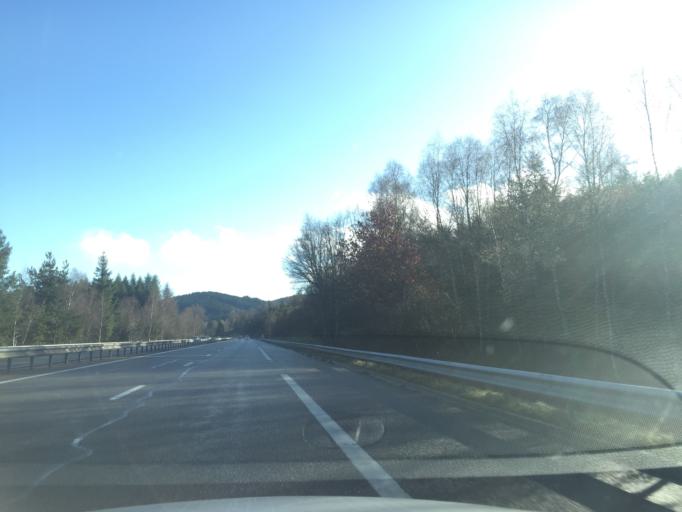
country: FR
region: Auvergne
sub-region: Departement du Puy-de-Dome
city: Chabreloche
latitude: 45.8736
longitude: 3.6968
